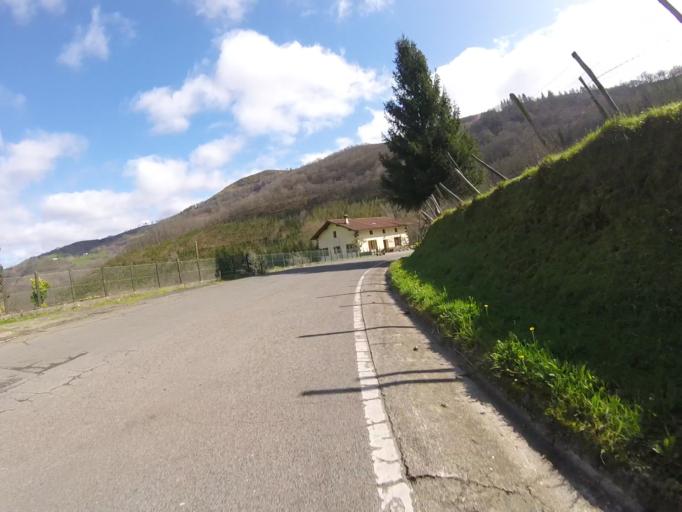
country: ES
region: Navarre
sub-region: Provincia de Navarra
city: Goizueta
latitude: 43.1492
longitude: -1.8509
